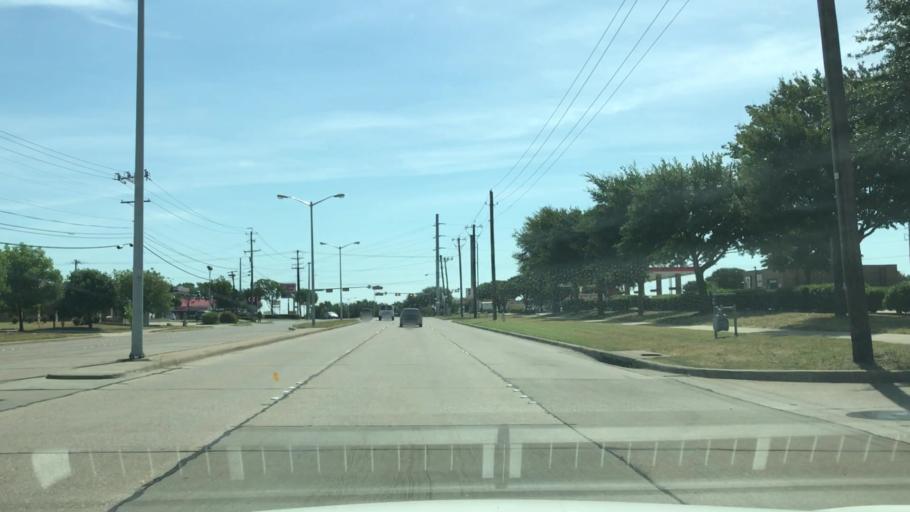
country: US
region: Texas
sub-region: Dallas County
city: Garland
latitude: 32.9446
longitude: -96.6673
